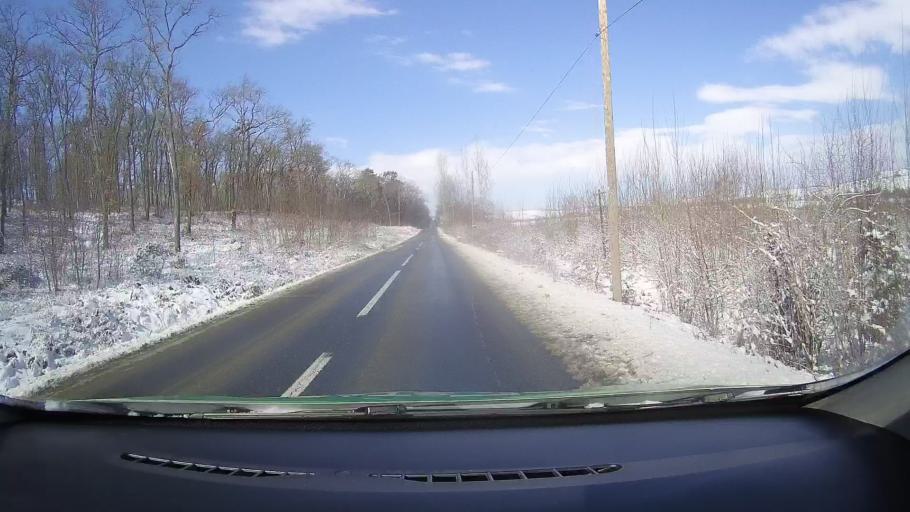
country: RO
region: Sibiu
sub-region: Comuna Nocrich
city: Nocrich
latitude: 45.8664
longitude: 24.4539
